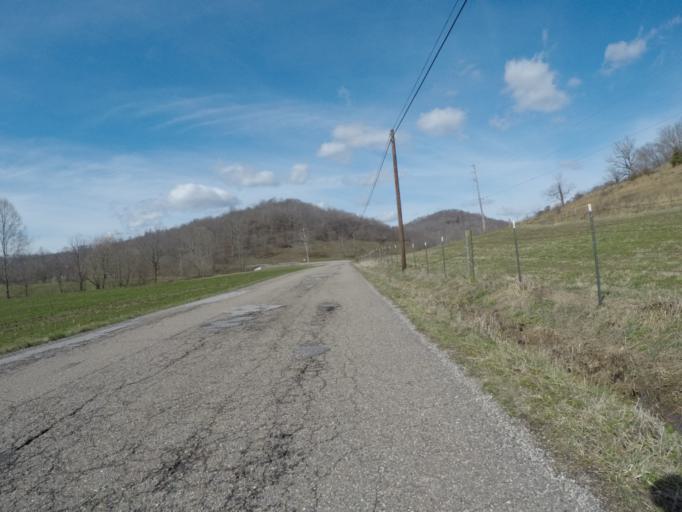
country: US
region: West Virginia
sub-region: Cabell County
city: Huntington
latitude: 38.4814
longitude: -82.4910
